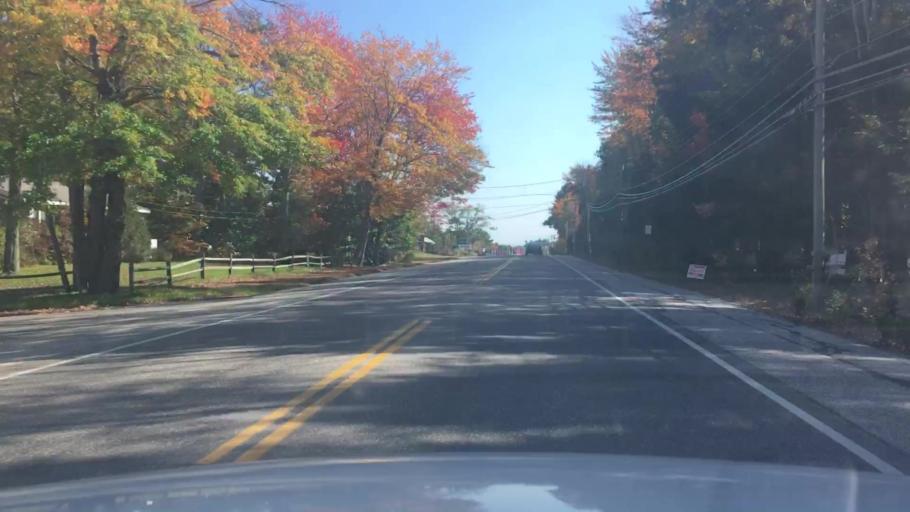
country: US
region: Maine
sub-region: Sagadahoc County
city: Topsham
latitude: 43.9466
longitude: -69.9866
